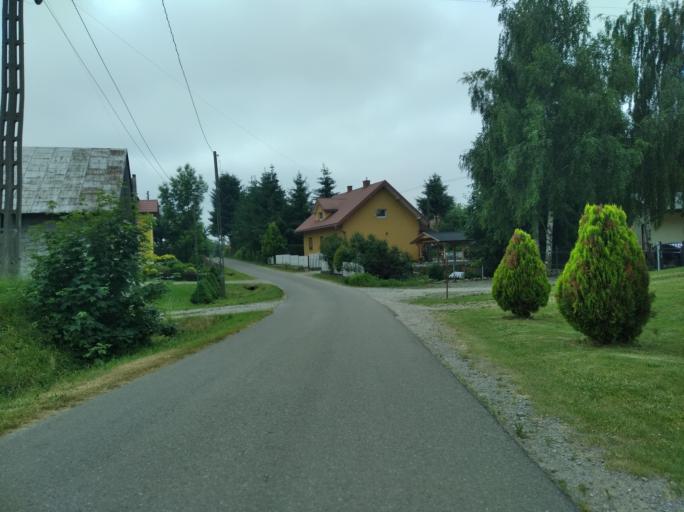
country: PL
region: Subcarpathian Voivodeship
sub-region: Powiat brzozowski
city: Jablonica Polska
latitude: 49.6826
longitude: 21.8891
